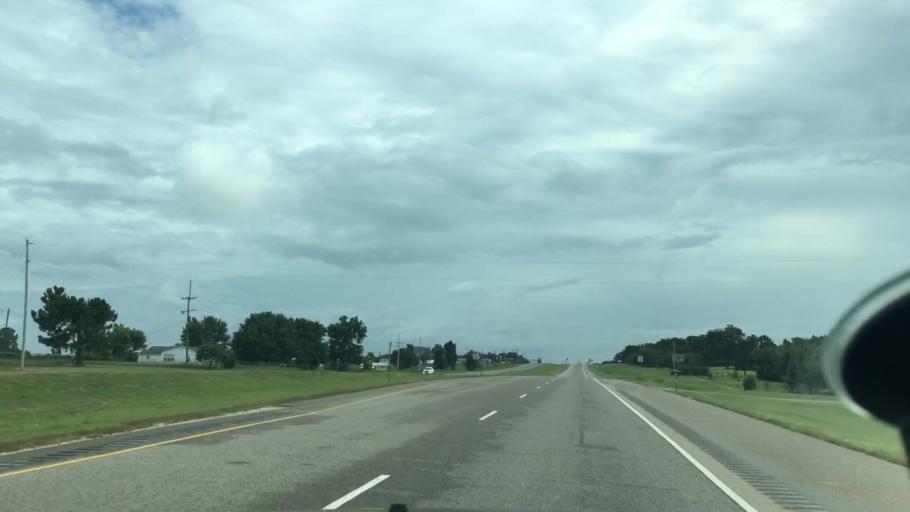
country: US
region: Oklahoma
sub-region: Lincoln County
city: Prague
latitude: 35.3562
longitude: -96.6718
